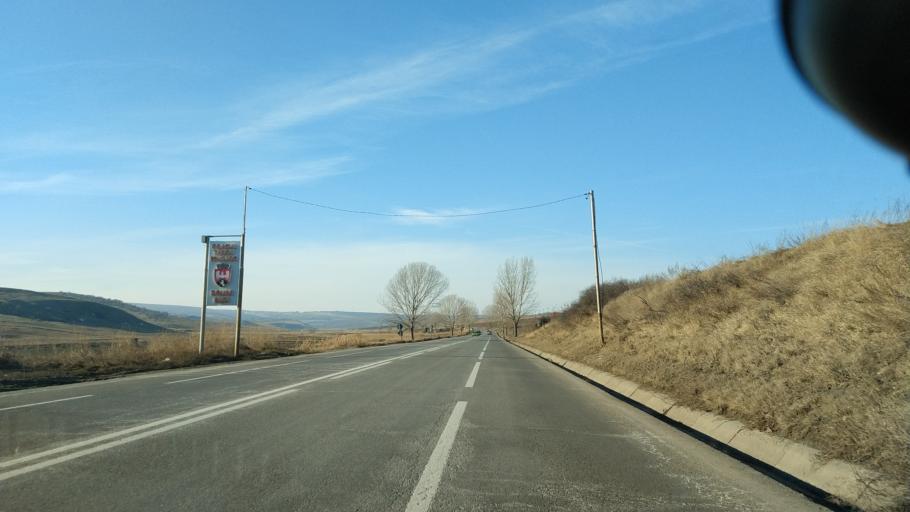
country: RO
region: Iasi
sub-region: Comuna Targu Frumos
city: Targu Frumos
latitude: 47.1955
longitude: 26.9947
